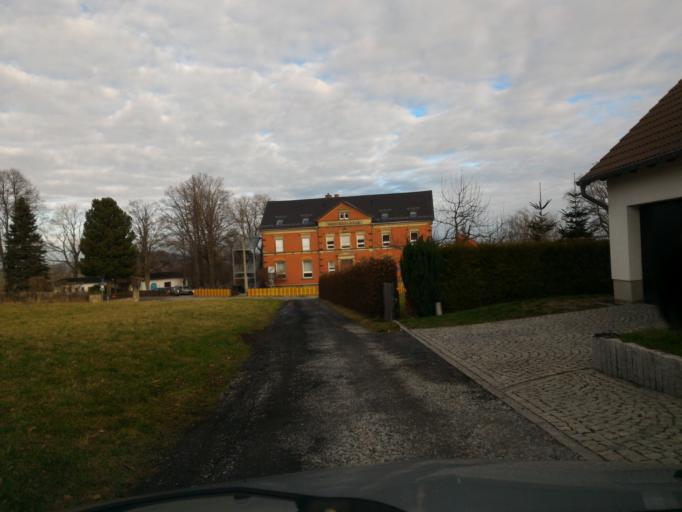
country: DE
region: Saxony
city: Grossschonau
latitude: 50.8699
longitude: 14.6483
